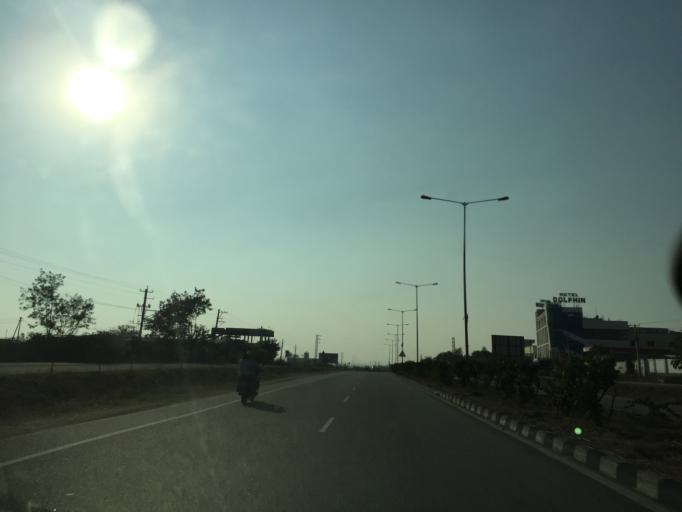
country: IN
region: Telangana
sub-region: Nalgonda
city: Bhongir
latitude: 17.5042
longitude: 78.8625
